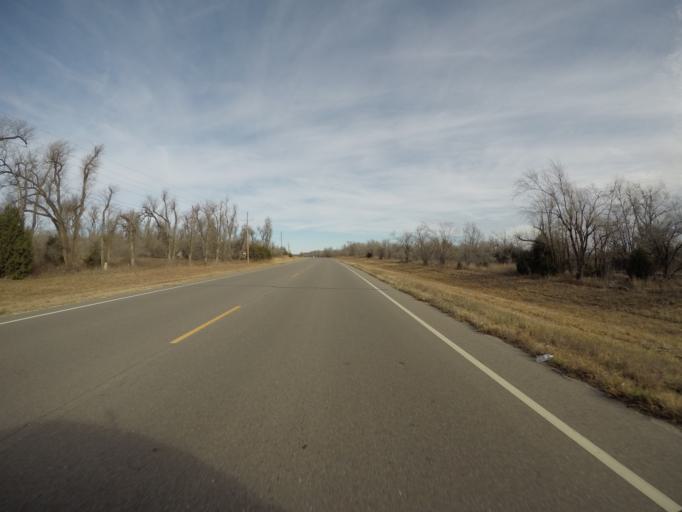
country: US
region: Kansas
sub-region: Reno County
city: Hutchinson
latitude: 38.1108
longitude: -97.8654
